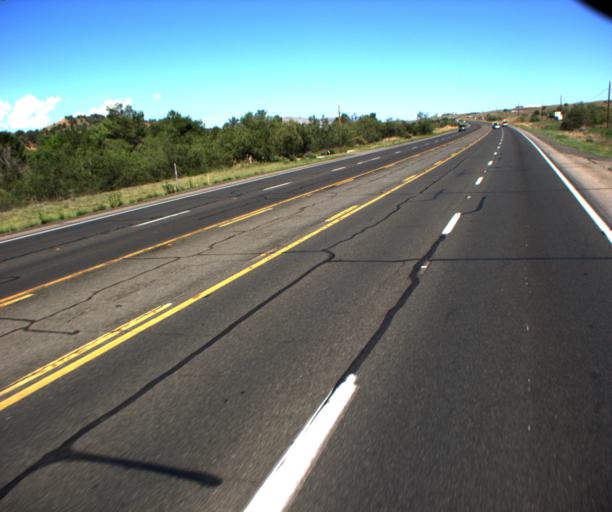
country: US
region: Arizona
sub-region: Yavapai County
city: Dewey-Humboldt
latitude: 34.5703
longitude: -112.2729
